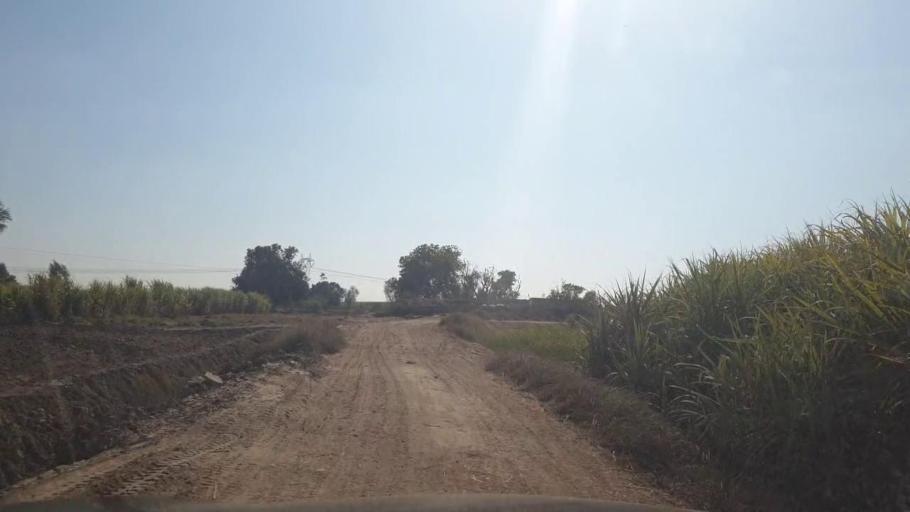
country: PK
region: Sindh
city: Adilpur
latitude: 27.9711
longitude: 69.4301
